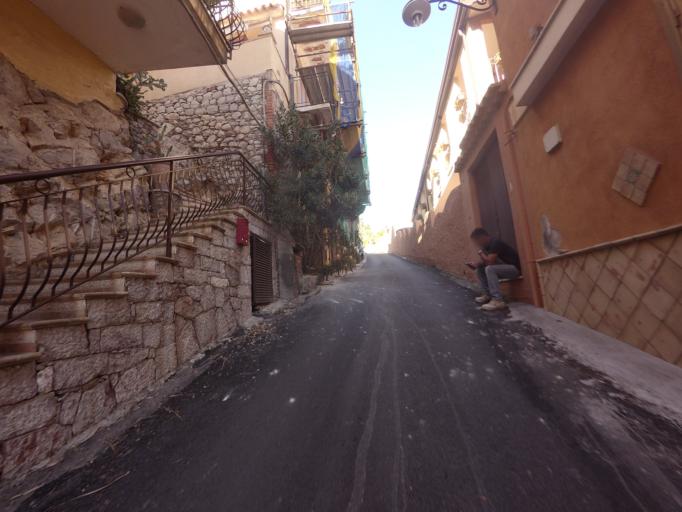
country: IT
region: Sicily
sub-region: Messina
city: Taormina
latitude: 37.8509
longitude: 15.2936
